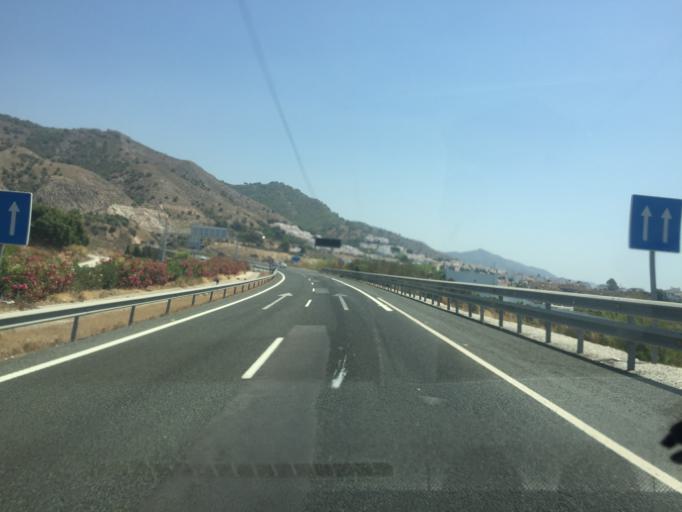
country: ES
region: Andalusia
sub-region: Provincia de Malaga
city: Nerja
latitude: 36.7639
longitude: -3.8815
